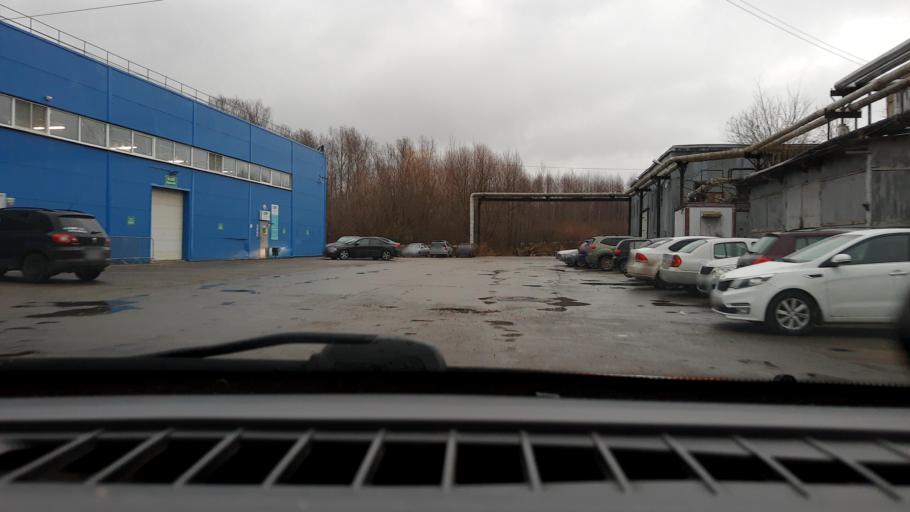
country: RU
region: Nizjnij Novgorod
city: Gorbatovka
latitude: 56.3085
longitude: 43.8307
